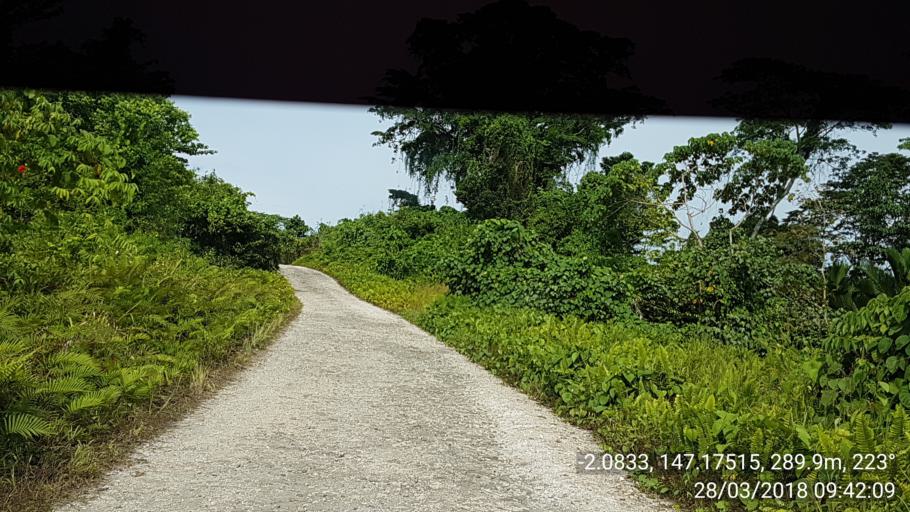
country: PG
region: Manus
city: Lorengau
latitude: -2.0833
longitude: 147.1748
